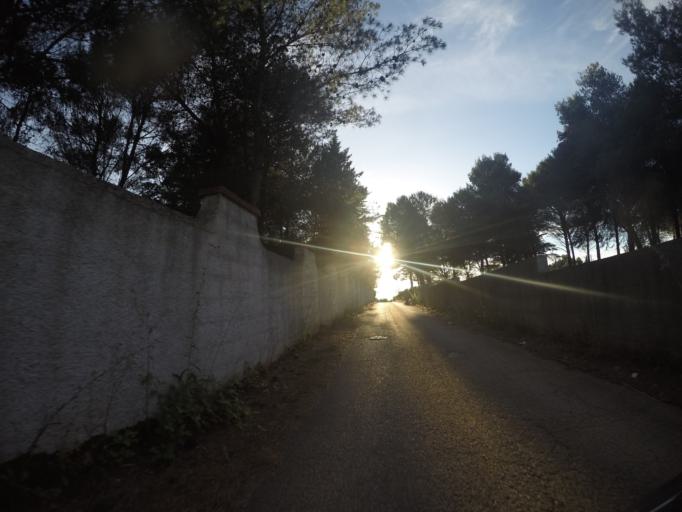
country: IT
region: Apulia
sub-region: Provincia di Taranto
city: Martina Franca
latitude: 40.6512
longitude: 17.3620
